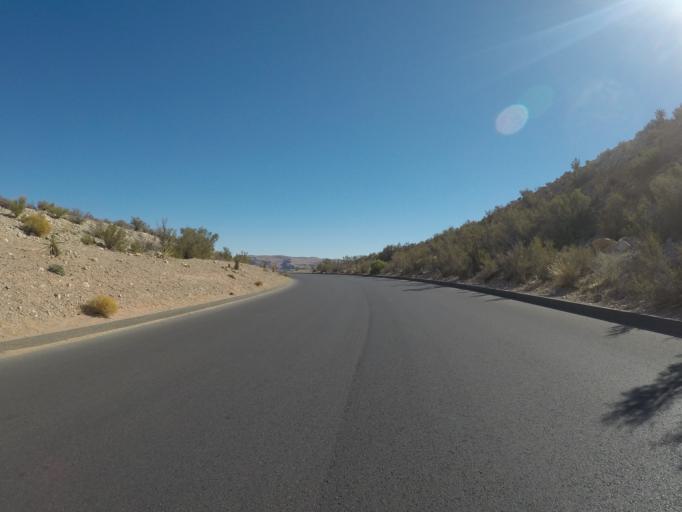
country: US
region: Nevada
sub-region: Clark County
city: Summerlin South
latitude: 36.1428
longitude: -115.4765
